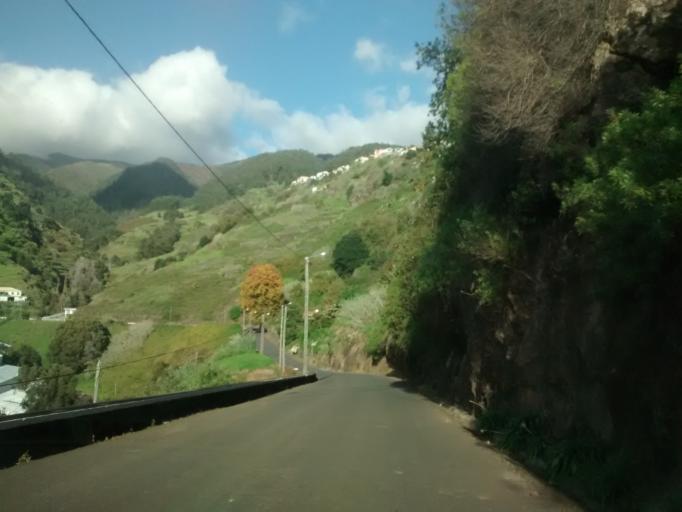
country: PT
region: Madeira
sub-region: Calheta
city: Estreito da Calheta
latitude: 32.7329
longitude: -17.1773
